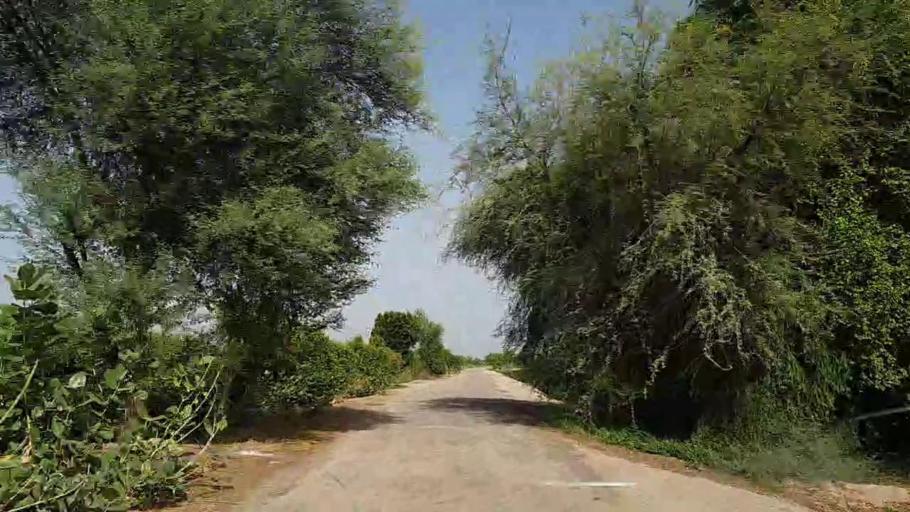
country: PK
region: Sindh
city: Kandiaro
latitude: 27.0727
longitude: 68.1449
